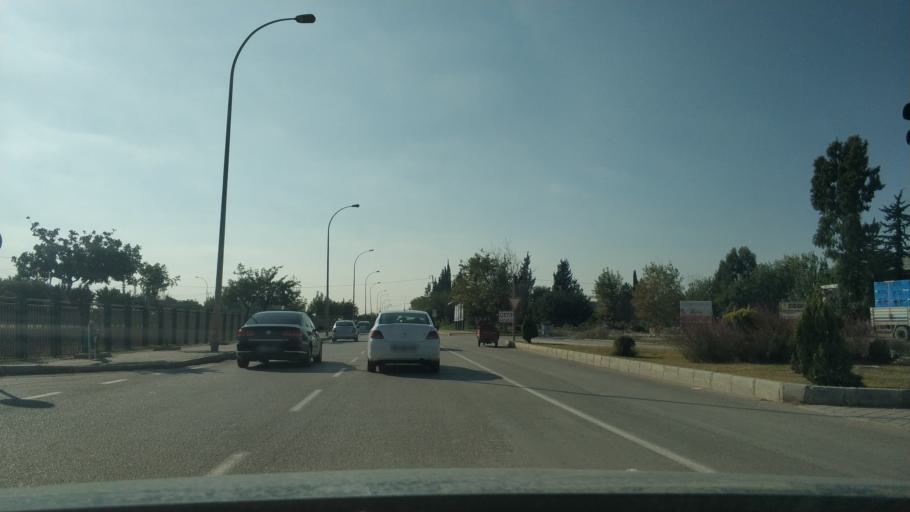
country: TR
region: Adana
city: Seyhan
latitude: 37.0076
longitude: 35.2575
